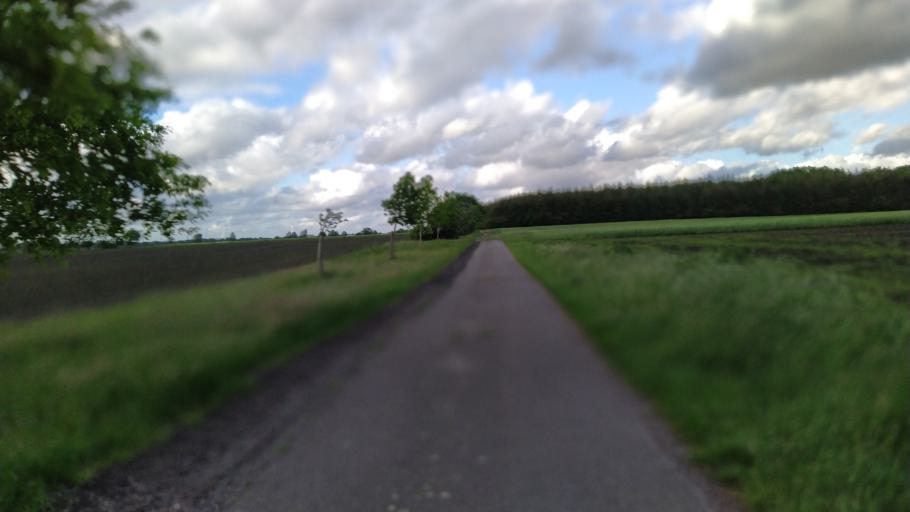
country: DE
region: Lower Saxony
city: Farven
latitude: 53.4541
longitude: 9.3005
